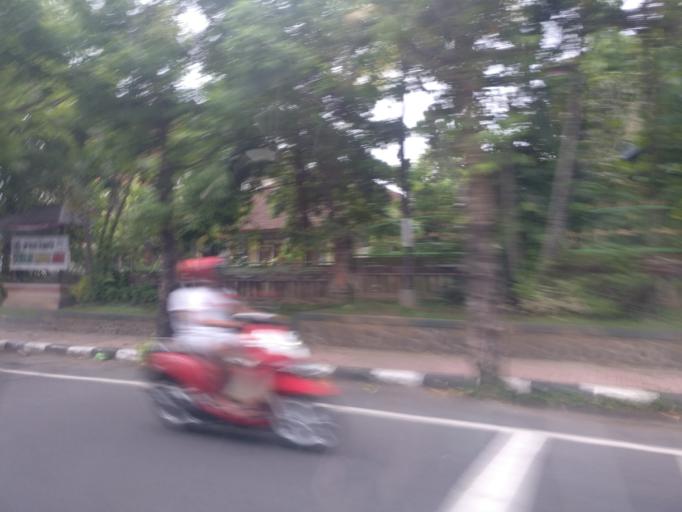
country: ID
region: Bali
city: Banjar Sedang
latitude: -8.5617
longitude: 115.3011
